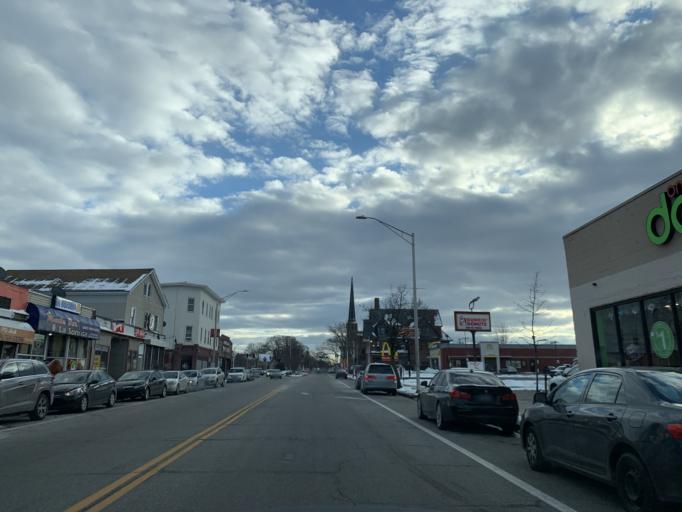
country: US
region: Rhode Island
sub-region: Providence County
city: Providence
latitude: 41.8147
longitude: -71.4210
